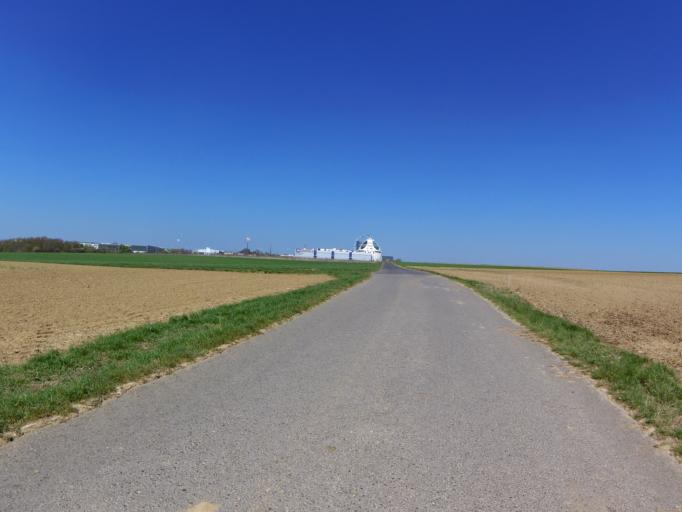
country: DE
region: Bavaria
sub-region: Regierungsbezirk Unterfranken
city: Biebelried
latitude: 49.7733
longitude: 10.0722
